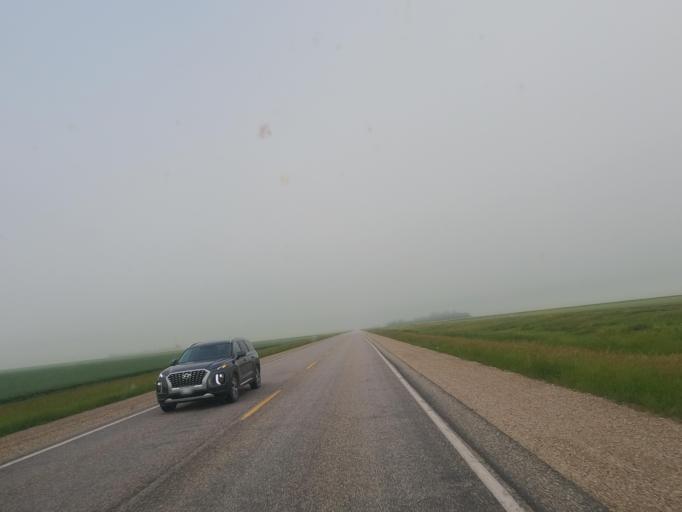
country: CA
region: Manitoba
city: Carman
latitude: 49.7218
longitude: -97.8860
